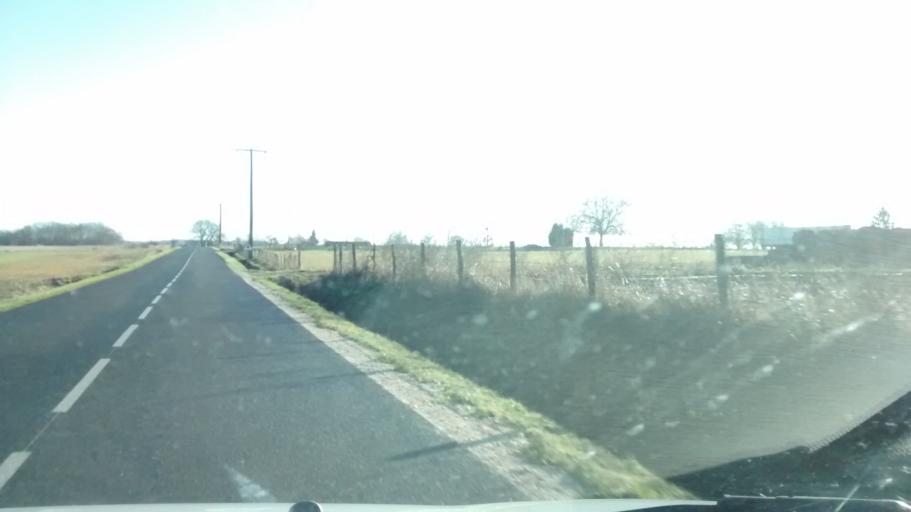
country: FR
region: Centre
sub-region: Departement d'Indre-et-Loire
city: Reugny
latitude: 47.4852
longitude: 0.8448
